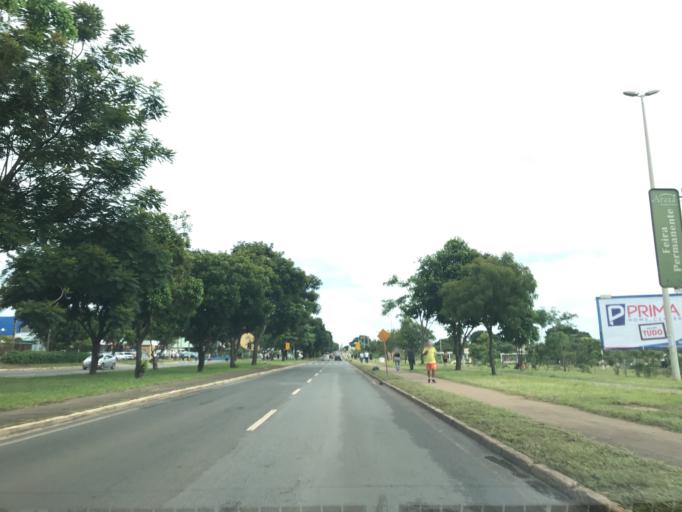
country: BR
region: Federal District
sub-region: Brasilia
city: Brasilia
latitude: -15.8251
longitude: -48.0849
